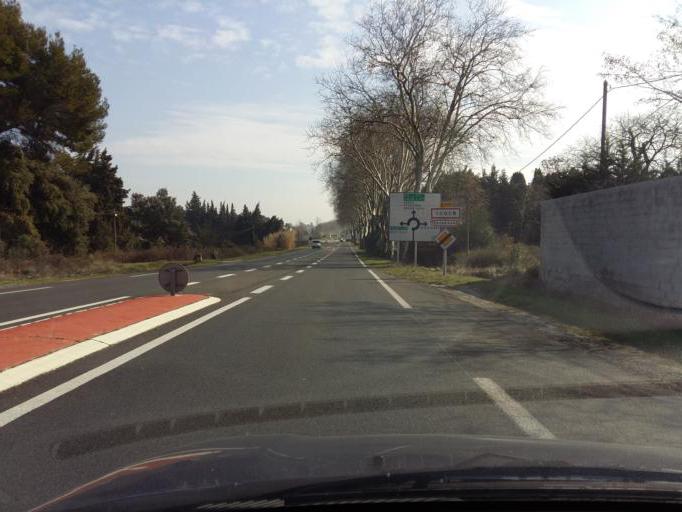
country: FR
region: Provence-Alpes-Cote d'Azur
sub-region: Departement des Bouches-du-Rhone
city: Orgon
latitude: 43.7938
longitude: 5.0245
